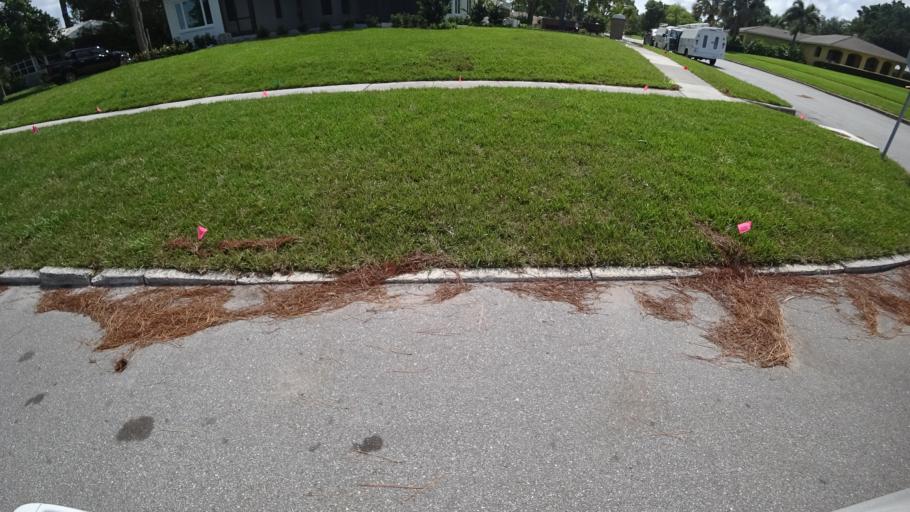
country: US
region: Florida
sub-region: Manatee County
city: Whitfield
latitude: 27.3990
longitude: -82.5697
